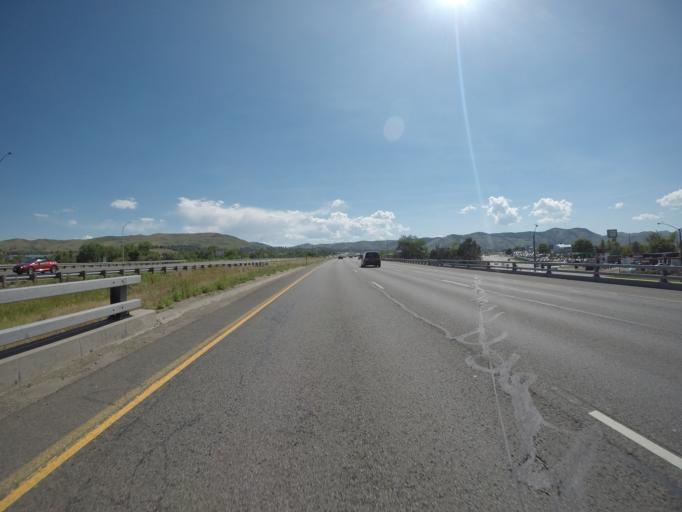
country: US
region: Colorado
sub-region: Jefferson County
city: West Pleasant View
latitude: 39.7304
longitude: -105.1715
